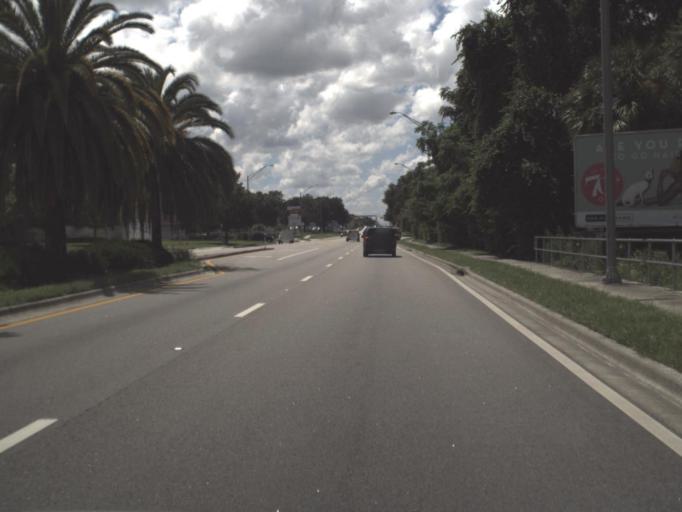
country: US
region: Florida
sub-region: Polk County
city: Gibsonia
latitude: 28.0812
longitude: -81.9534
